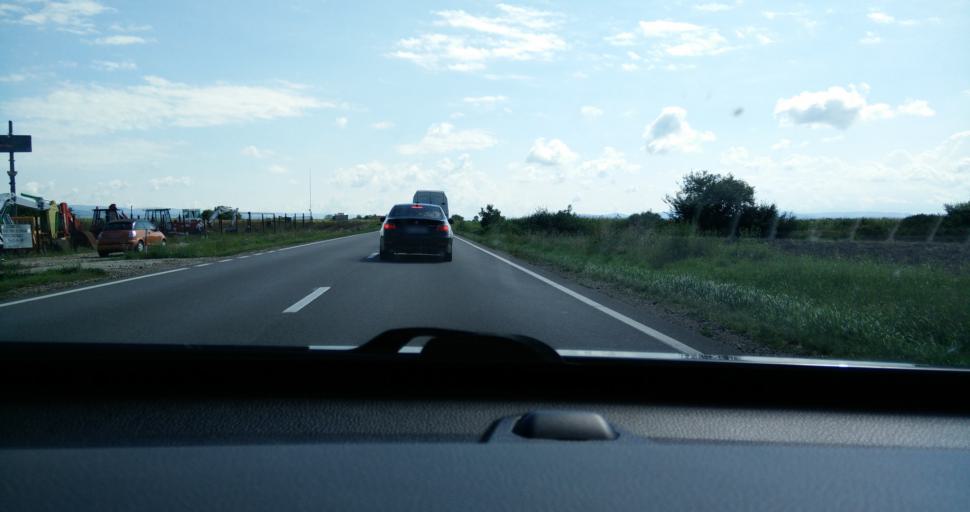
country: RO
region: Bihor
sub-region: Comuna Osorheiu
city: Osorheiu
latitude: 47.0544
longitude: 22.0819
